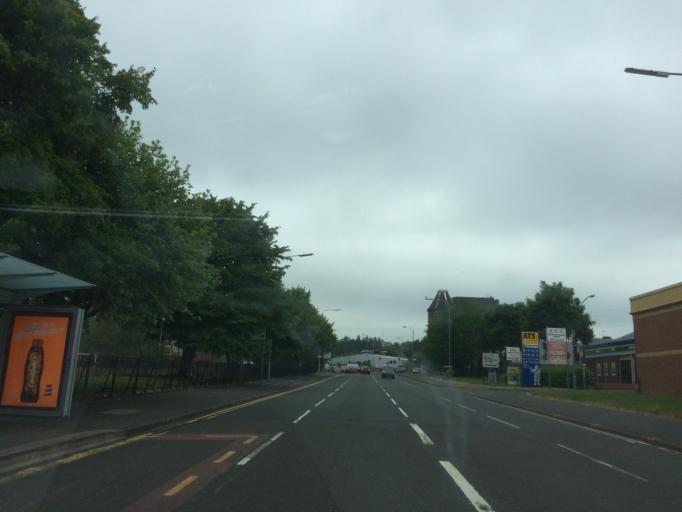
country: GB
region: Scotland
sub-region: Glasgow City
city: Glasgow
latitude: 55.8729
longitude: -4.2611
